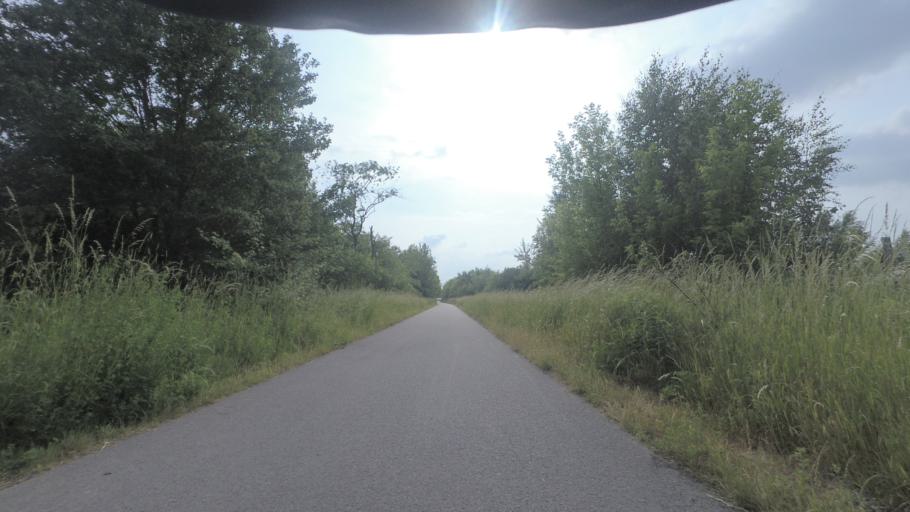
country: DE
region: Berlin
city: Lichtenrade
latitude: 52.4125
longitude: 13.4315
